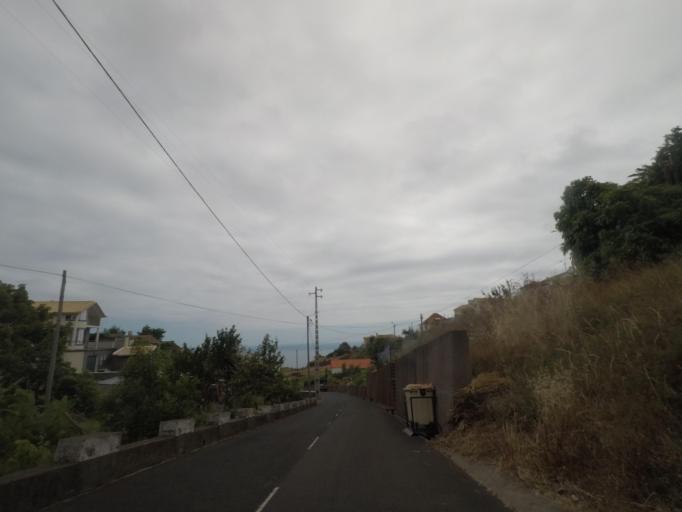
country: PT
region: Madeira
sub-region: Calheta
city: Estreito da Calheta
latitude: 32.7370
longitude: -17.1717
